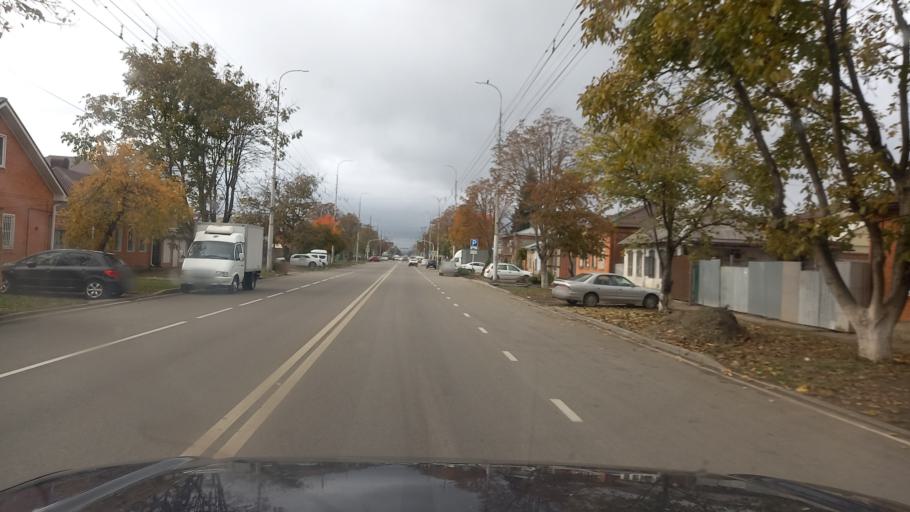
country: RU
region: Adygeya
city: Maykop
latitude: 44.6081
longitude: 40.1163
